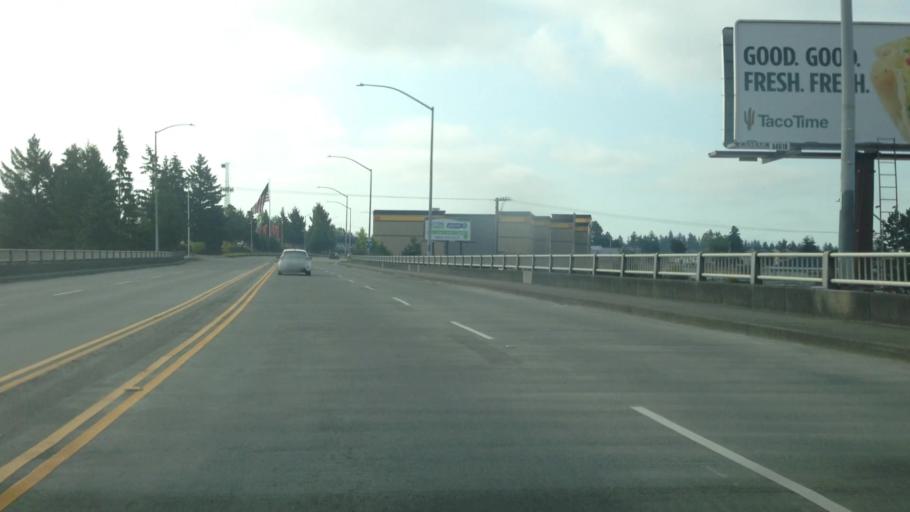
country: US
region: Washington
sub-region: Pierce County
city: Fircrest
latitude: 47.2248
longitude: -122.4831
